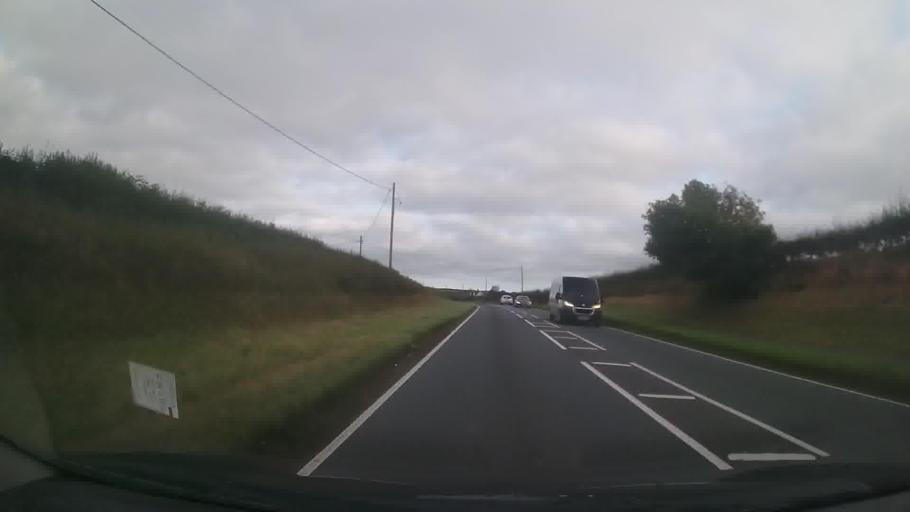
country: GB
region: Wales
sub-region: Pembrokeshire
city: Neyland
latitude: 51.7260
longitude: -4.9791
